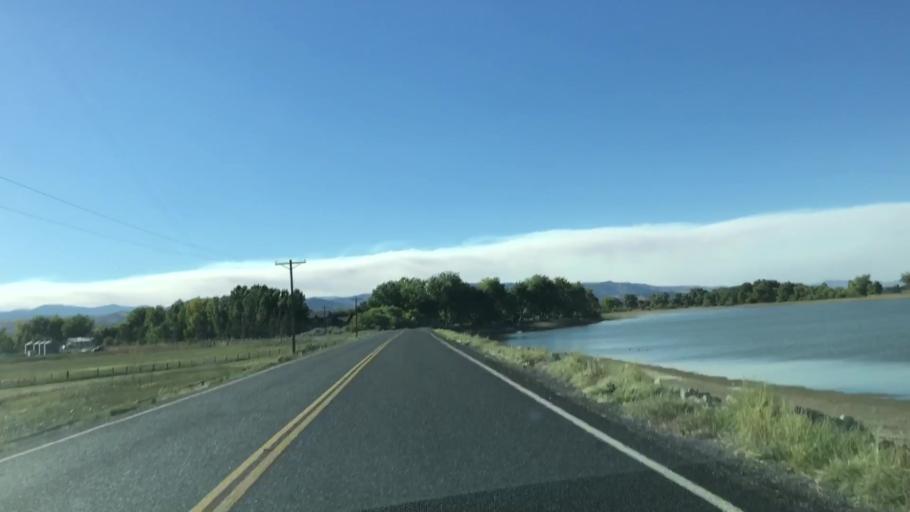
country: US
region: Colorado
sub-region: Larimer County
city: Loveland
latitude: 40.4611
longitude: -105.0536
